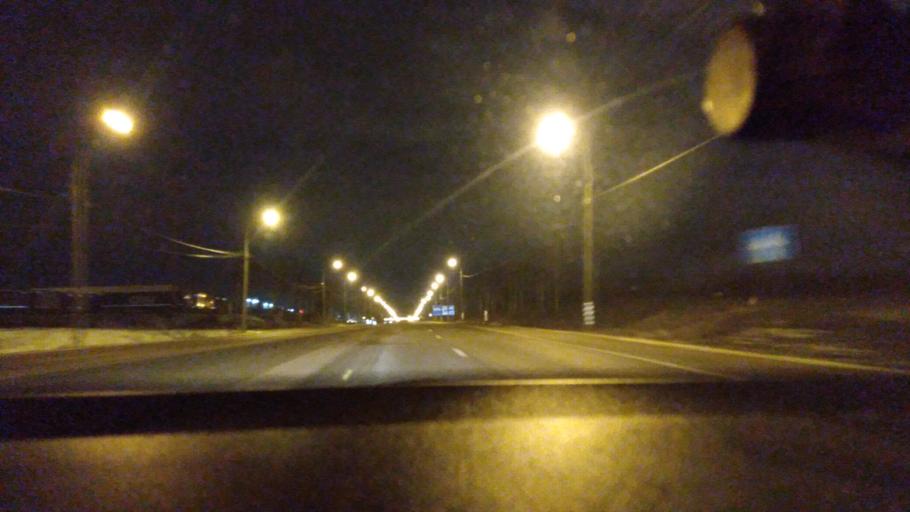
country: RU
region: Moskovskaya
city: Raduzhnyy
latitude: 55.1576
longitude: 38.6904
